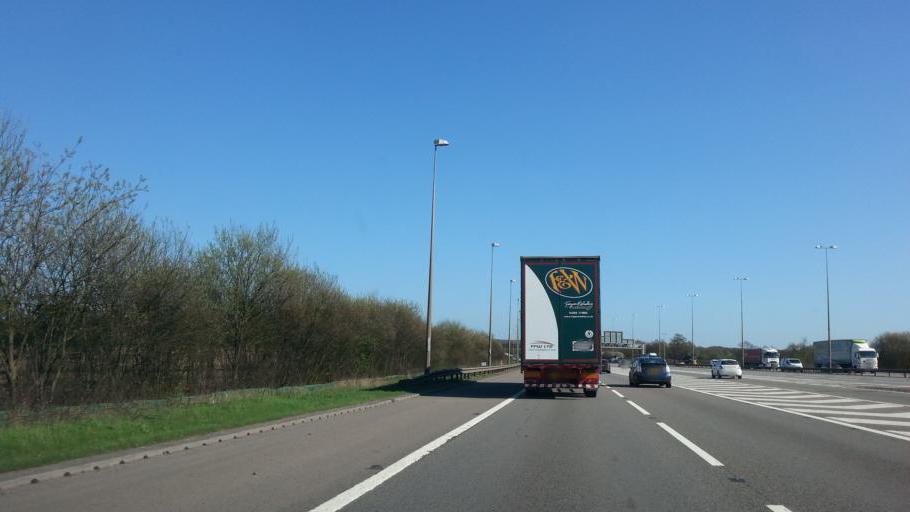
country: GB
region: England
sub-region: Solihull
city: Meriden
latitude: 52.4745
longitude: -1.6723
